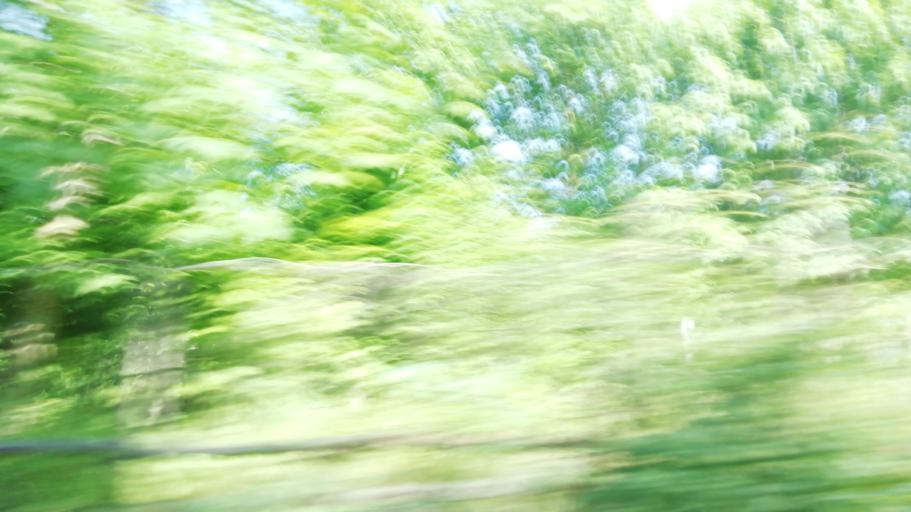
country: TR
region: Karabuk
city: Karabuk
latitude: 41.0859
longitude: 32.5816
